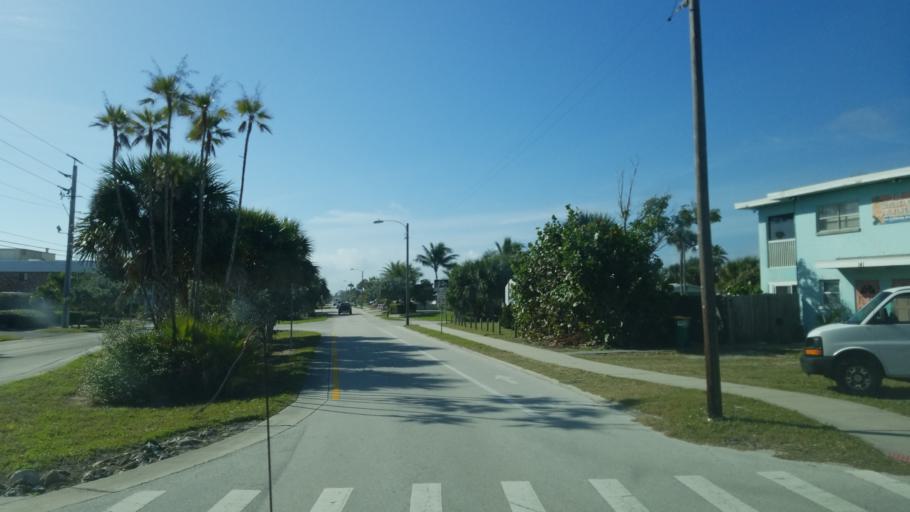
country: US
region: Florida
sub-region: Brevard County
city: Cape Canaveral
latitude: 28.3655
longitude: -80.6044
